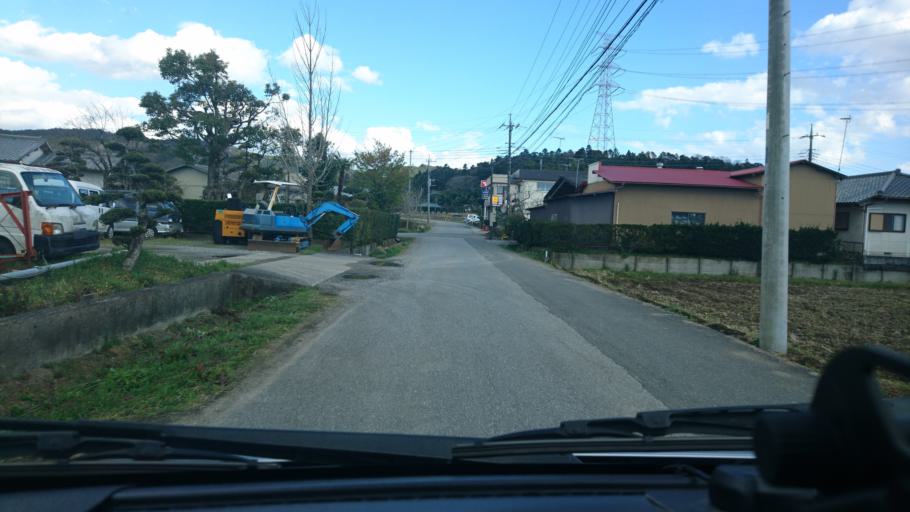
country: JP
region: Chiba
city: Kimitsu
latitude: 35.2870
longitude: 139.9876
